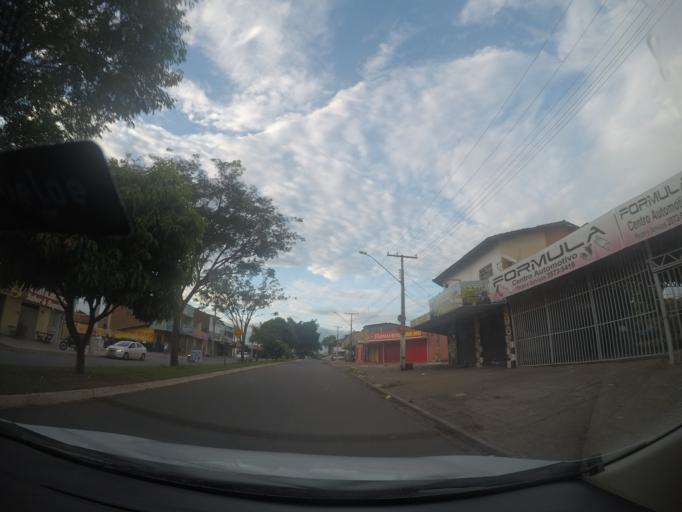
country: BR
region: Goias
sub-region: Goiania
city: Goiania
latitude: -16.6942
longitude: -49.3507
